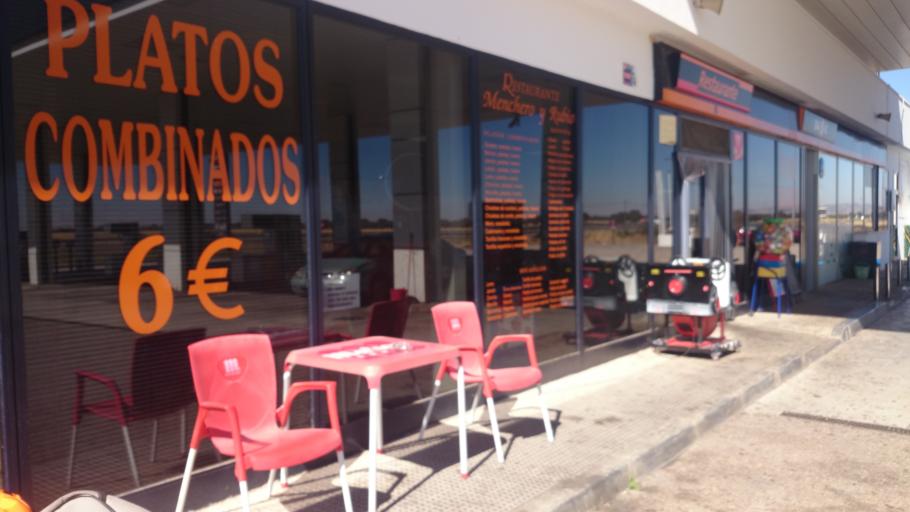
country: ES
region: Castille-La Mancha
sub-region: Provincia de Ciudad Real
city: Villarta de San Juan
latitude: 39.1802
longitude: -3.3991
